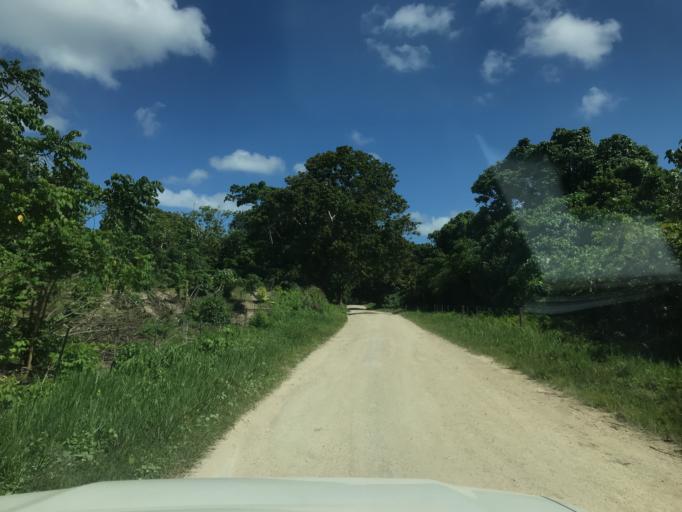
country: VU
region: Sanma
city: Luganville
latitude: -15.5790
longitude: 167.0349
